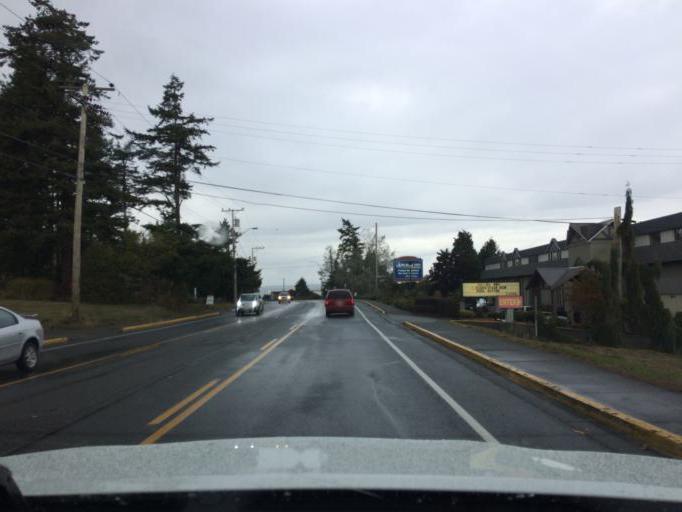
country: CA
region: British Columbia
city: Campbell River
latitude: 50.0115
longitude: -125.2341
